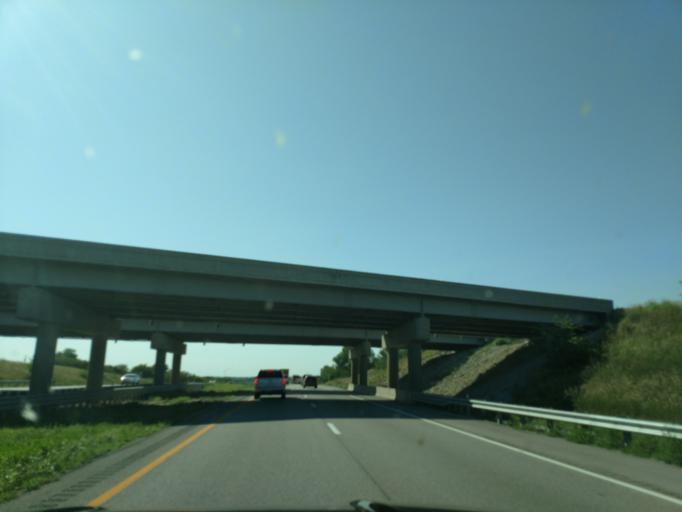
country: US
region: Missouri
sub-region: Andrew County
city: Country Club Village
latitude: 39.8579
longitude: -94.8102
